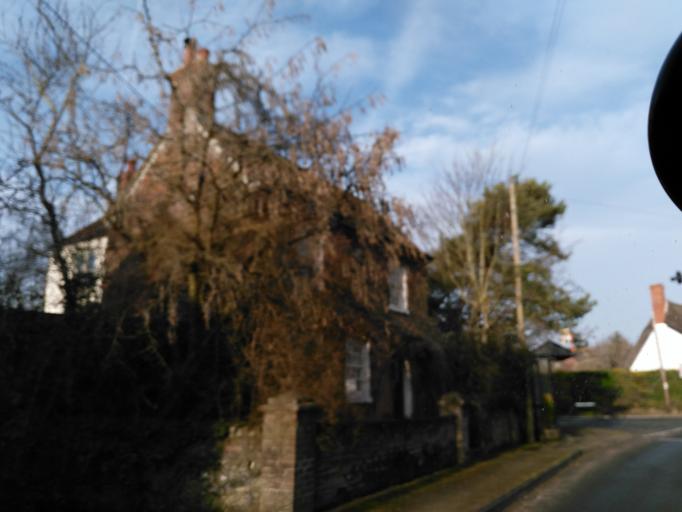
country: GB
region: England
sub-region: Wiltshire
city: Market Lavington
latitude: 51.2795
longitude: -1.9954
